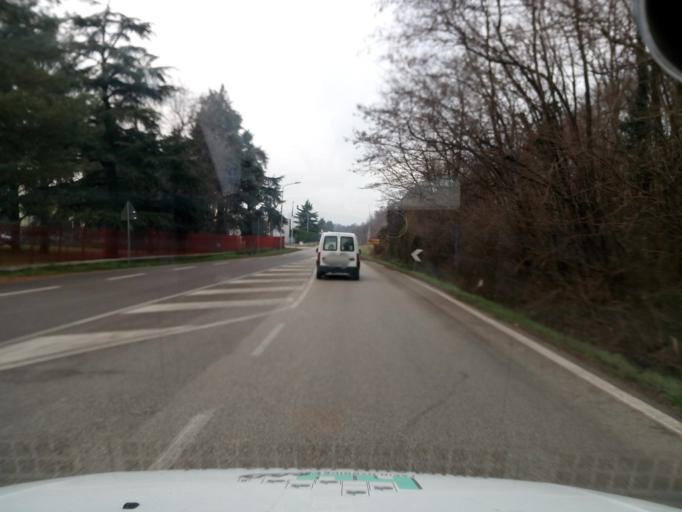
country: IT
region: Veneto
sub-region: Provincia di Vicenza
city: Zermeghedo
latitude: 45.4781
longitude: 11.3813
